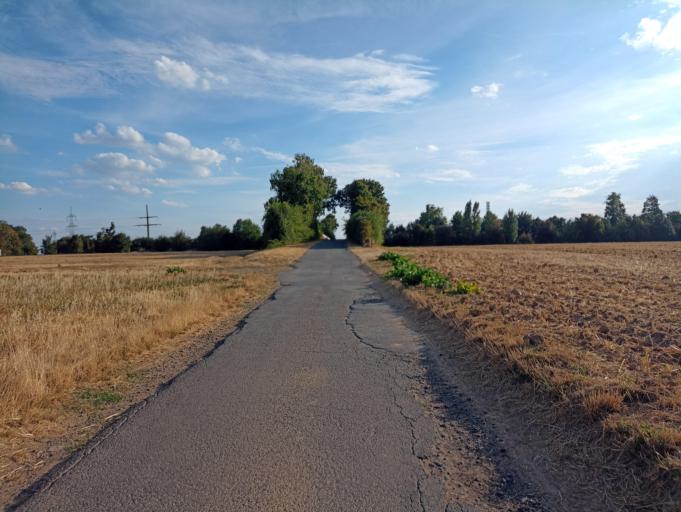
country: DE
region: Hesse
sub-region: Regierungsbezirk Darmstadt
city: Bad Homburg vor der Hoehe
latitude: 50.2041
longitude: 8.6415
